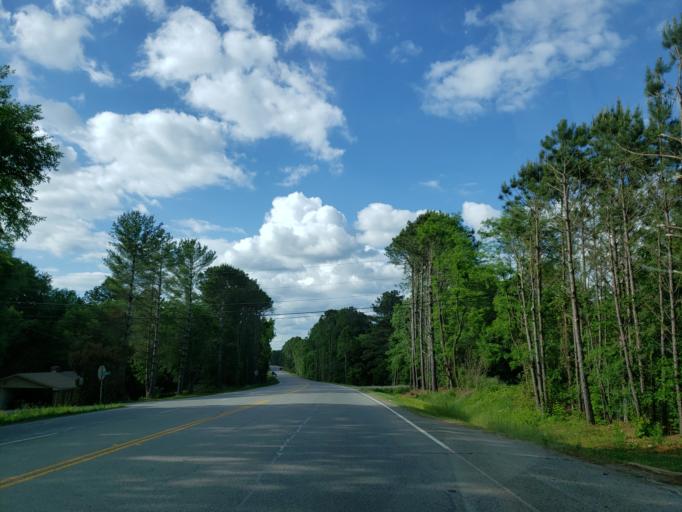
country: US
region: Georgia
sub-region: Bartow County
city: Cartersville
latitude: 34.2498
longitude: -84.8574
